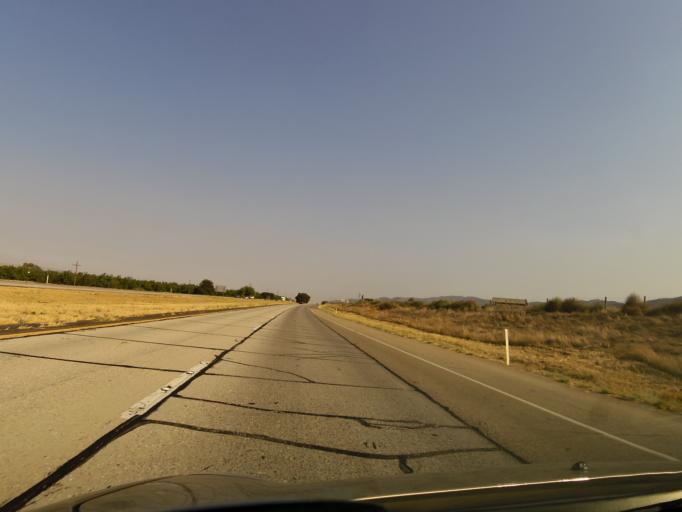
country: US
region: California
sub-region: San Luis Obispo County
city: Lake Nacimiento
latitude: 36.0099
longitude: -120.9198
